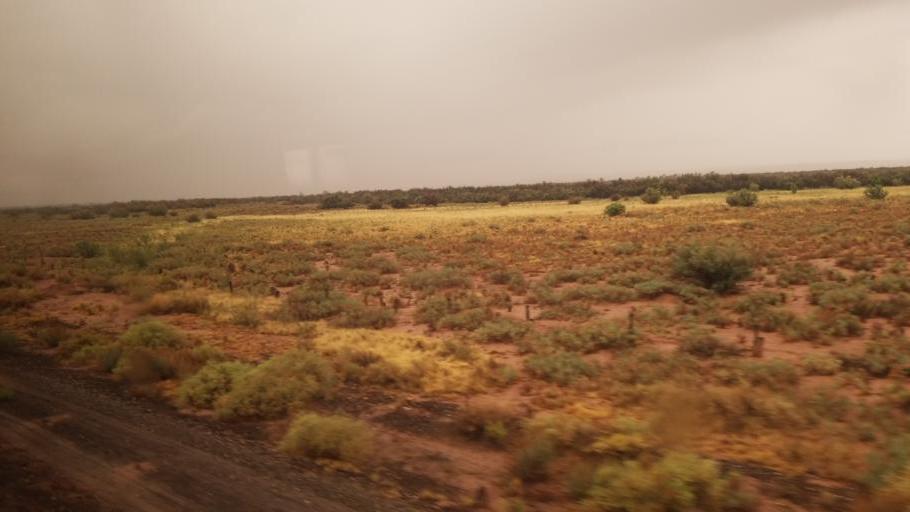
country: US
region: Arizona
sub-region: Navajo County
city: Joseph City
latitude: 34.9674
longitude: -110.4780
